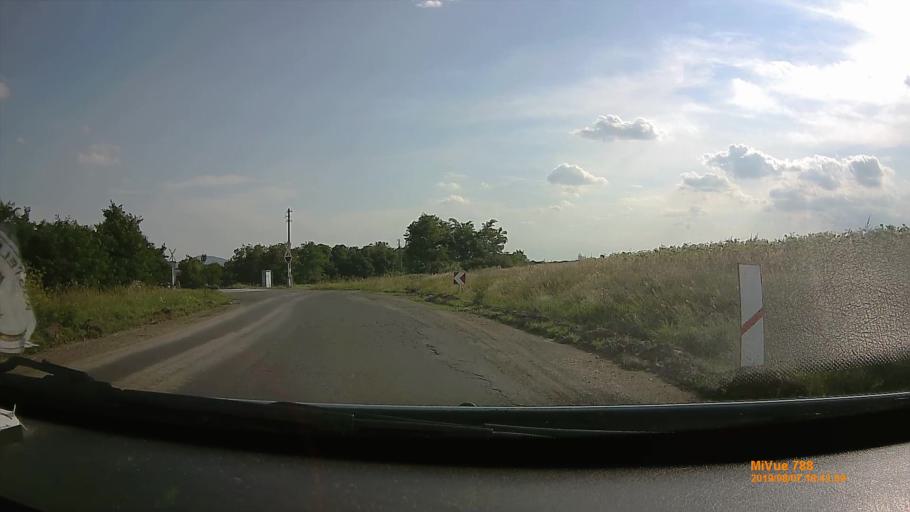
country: HU
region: Borsod-Abauj-Zemplen
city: Abaujszanto
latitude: 48.3497
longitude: 21.2119
